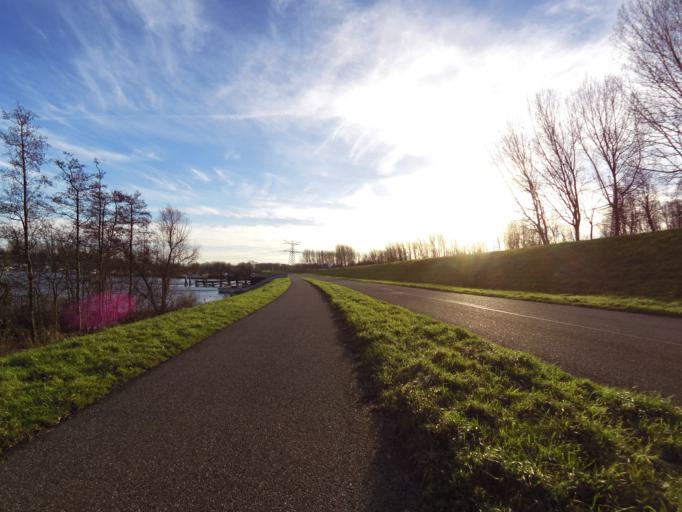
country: NL
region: South Holland
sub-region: Gemeente Rotterdam
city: Hoek van Holland
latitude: 51.9267
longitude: 4.1031
